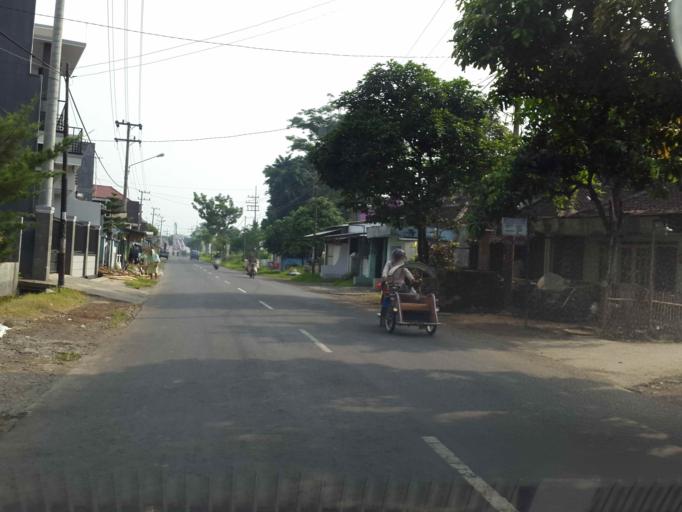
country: ID
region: East Java
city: Tamiajeng
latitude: -7.9636
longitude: 112.6946
